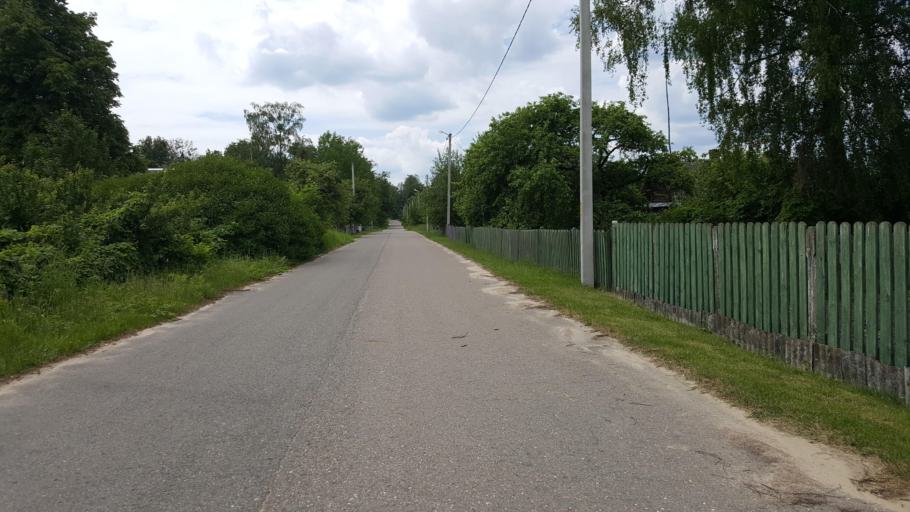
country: PL
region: Podlasie
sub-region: Powiat hajnowski
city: Bialowieza
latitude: 52.6268
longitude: 24.0817
